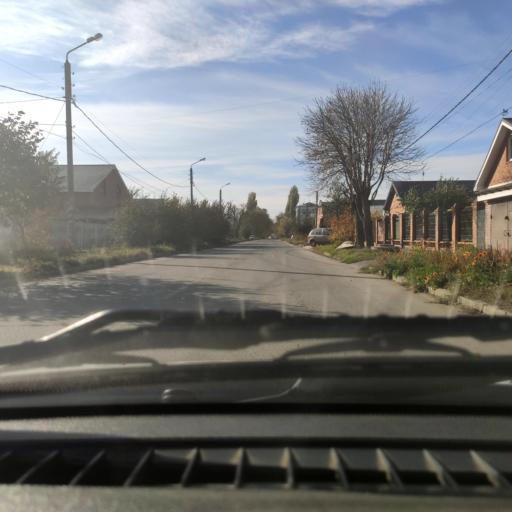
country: RU
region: Samara
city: Tol'yatti
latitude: 53.5359
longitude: 49.4158
